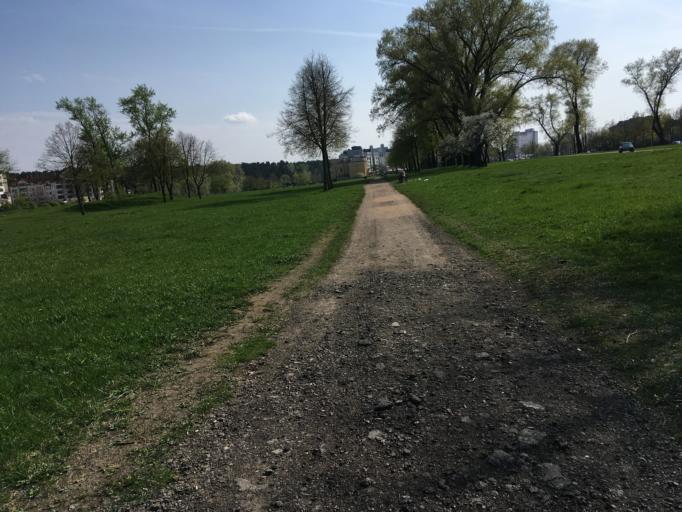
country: BY
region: Minsk
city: Minsk
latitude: 53.9230
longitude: 27.6397
